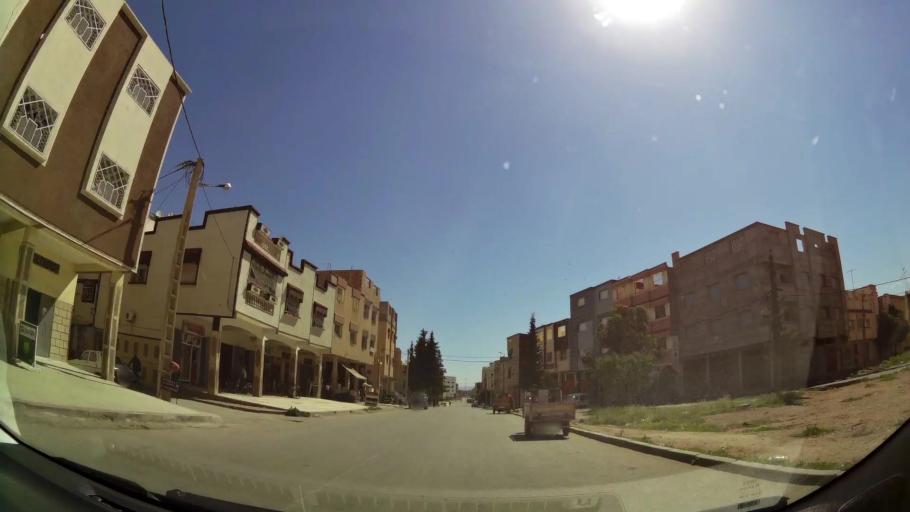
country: MA
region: Oriental
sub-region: Oujda-Angad
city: Oujda
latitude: 34.6597
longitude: -1.8913
